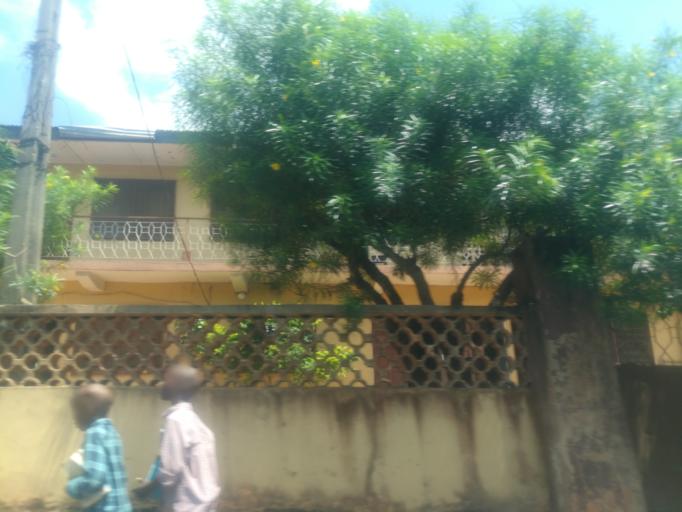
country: NG
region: Oyo
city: Ibadan
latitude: 7.3539
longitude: 3.8650
